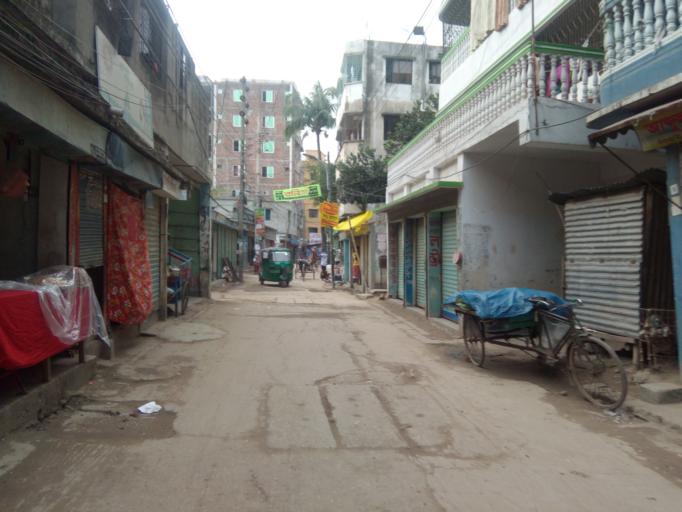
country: BD
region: Dhaka
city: Paltan
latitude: 23.7570
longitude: 90.4321
